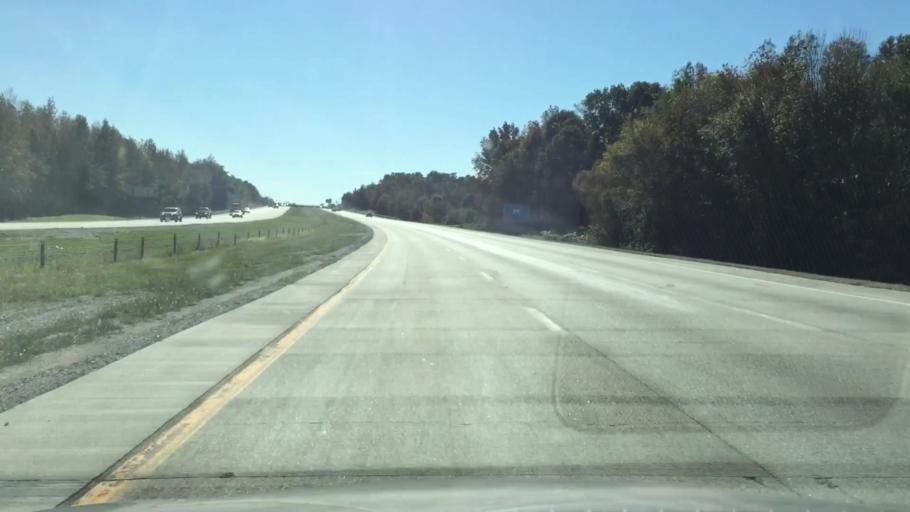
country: US
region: North Carolina
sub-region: Randolph County
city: Archdale
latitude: 35.9141
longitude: -79.9483
